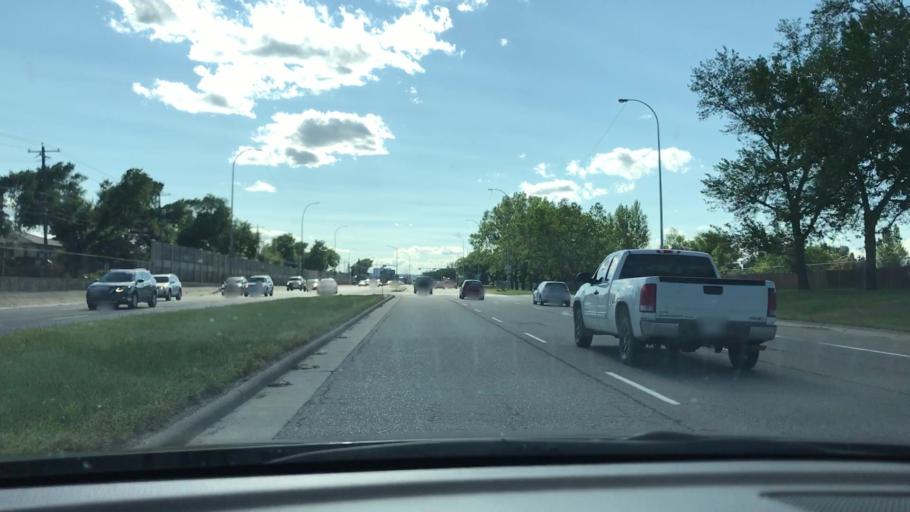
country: CA
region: Alberta
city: Calgary
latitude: 51.0670
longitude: -114.0381
